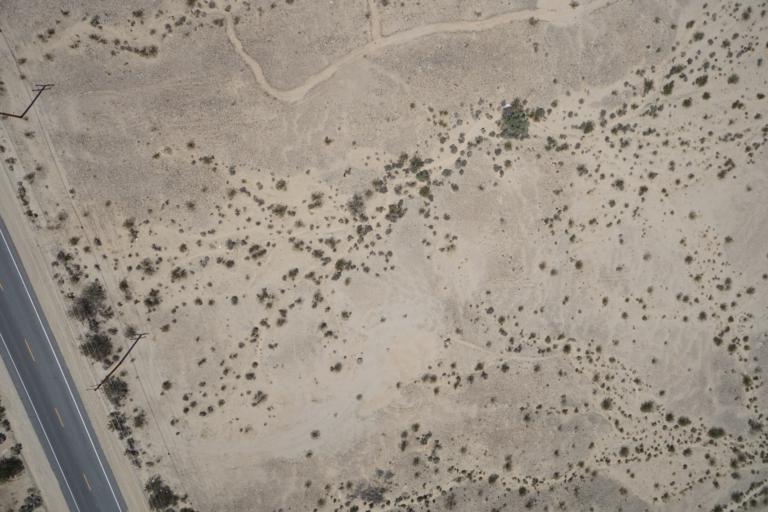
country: US
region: California
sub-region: San Bernardino County
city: Twentynine Palms
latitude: 34.1365
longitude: -116.0303
